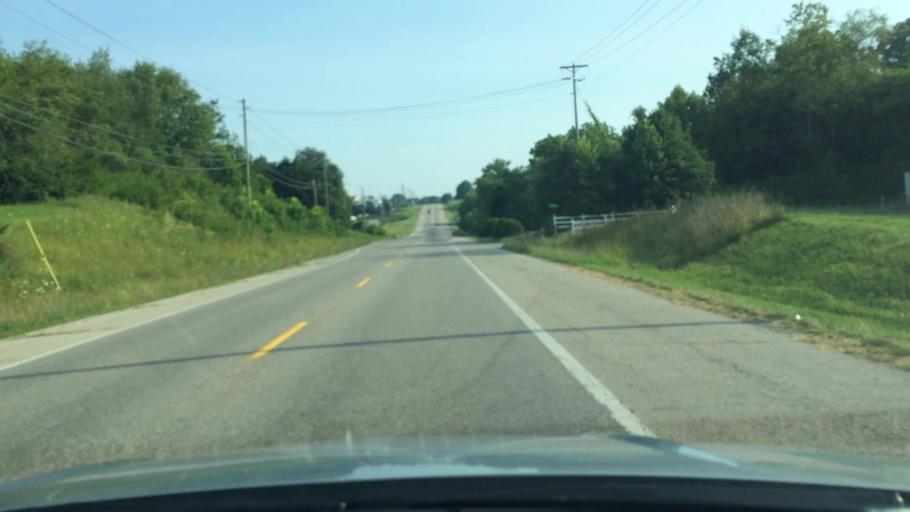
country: US
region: Tennessee
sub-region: Blount County
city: Maryville
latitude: 35.7473
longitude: -84.0442
